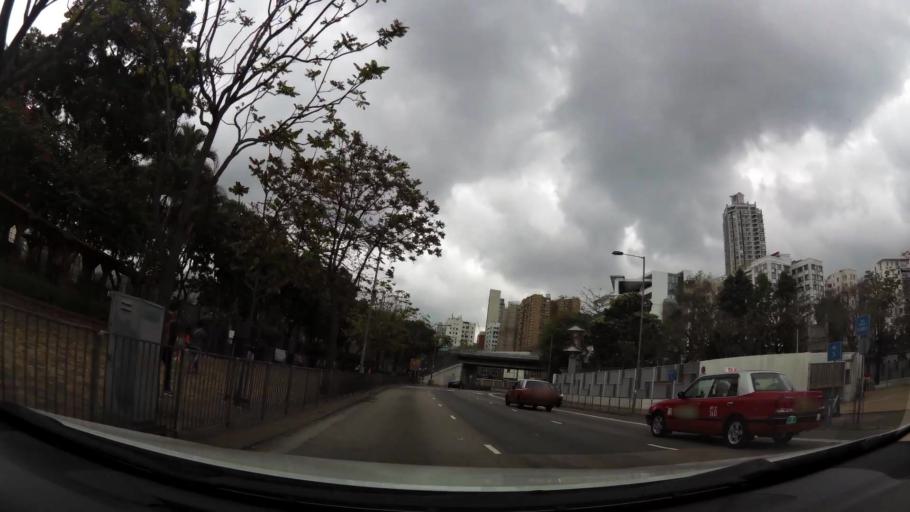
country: HK
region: Kowloon City
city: Kowloon
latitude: 22.3269
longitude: 114.1736
